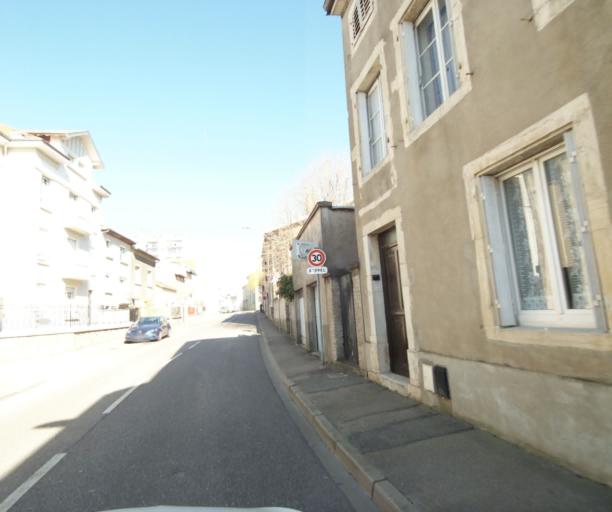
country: FR
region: Lorraine
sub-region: Departement de Meurthe-et-Moselle
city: Malzeville
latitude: 48.7102
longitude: 6.1845
